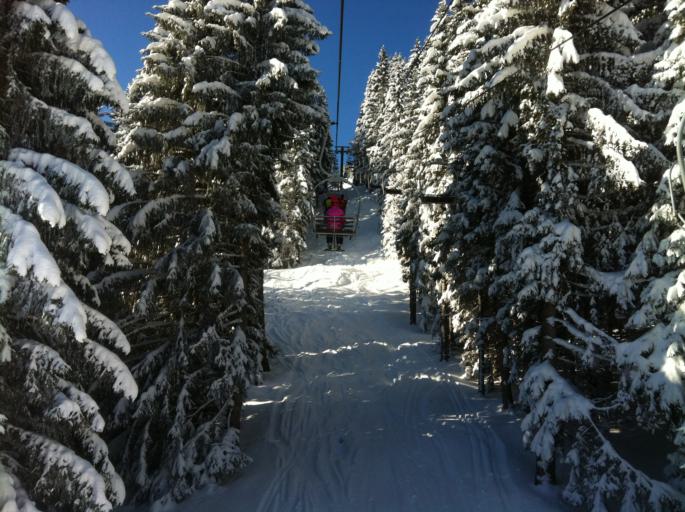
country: FR
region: Rhone-Alpes
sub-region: Departement de la Haute-Savoie
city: Saint-Gervais-les-Bains
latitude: 45.8570
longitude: 6.7110
